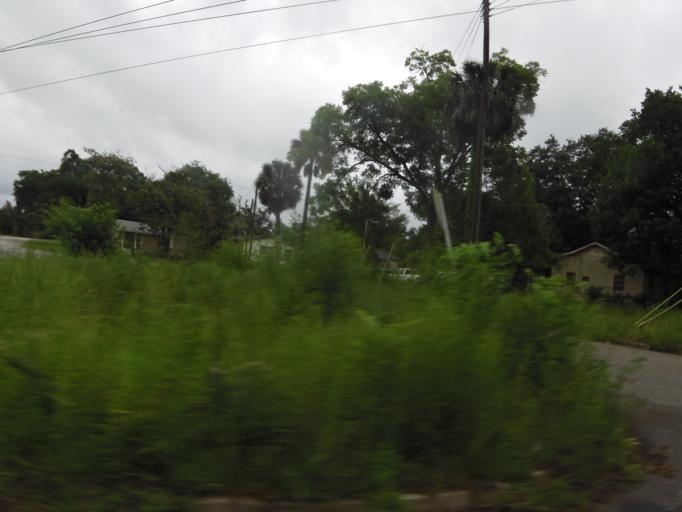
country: US
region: Florida
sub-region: Duval County
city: Jacksonville
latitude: 30.3507
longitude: -81.6328
